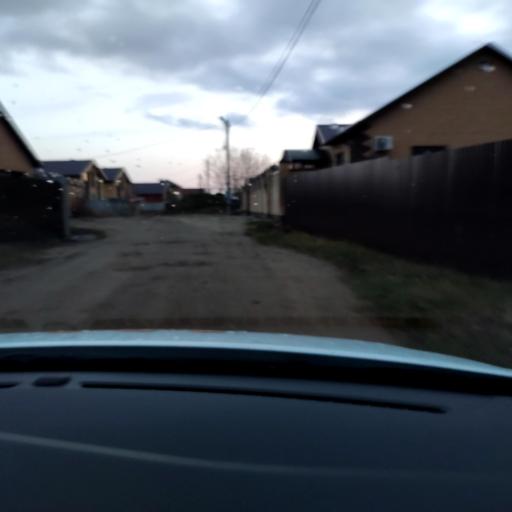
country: RU
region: Tatarstan
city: Stolbishchi
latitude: 55.6947
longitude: 49.1565
